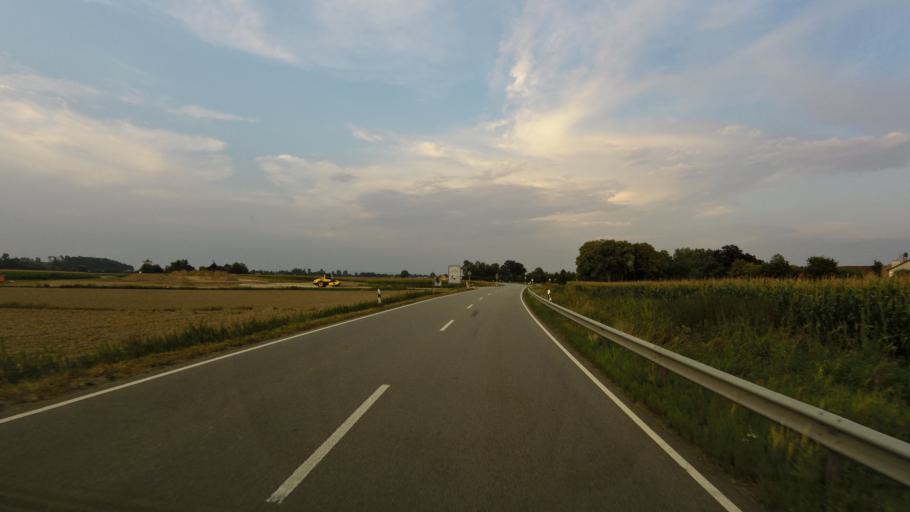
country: DE
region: Bavaria
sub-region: Lower Bavaria
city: Kirchham
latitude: 48.3387
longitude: 13.2369
